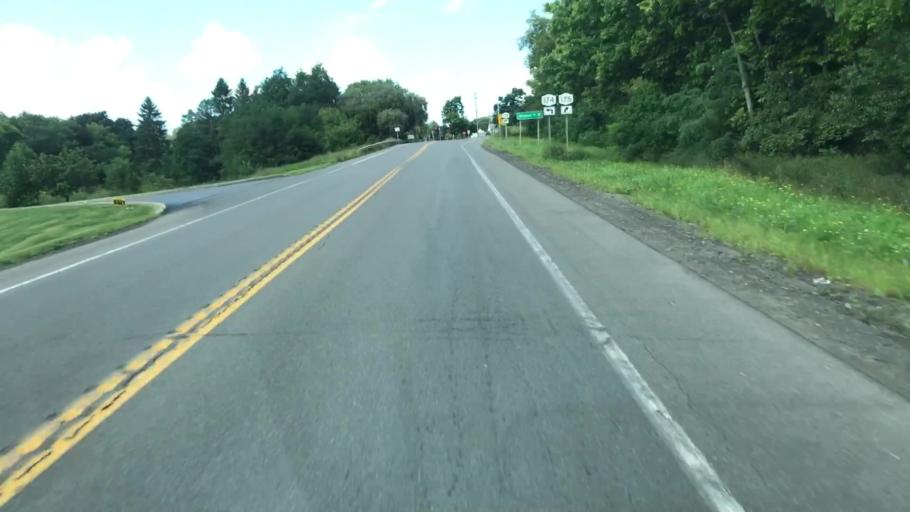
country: US
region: New York
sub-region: Onondaga County
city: Marcellus
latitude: 42.9805
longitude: -76.3312
